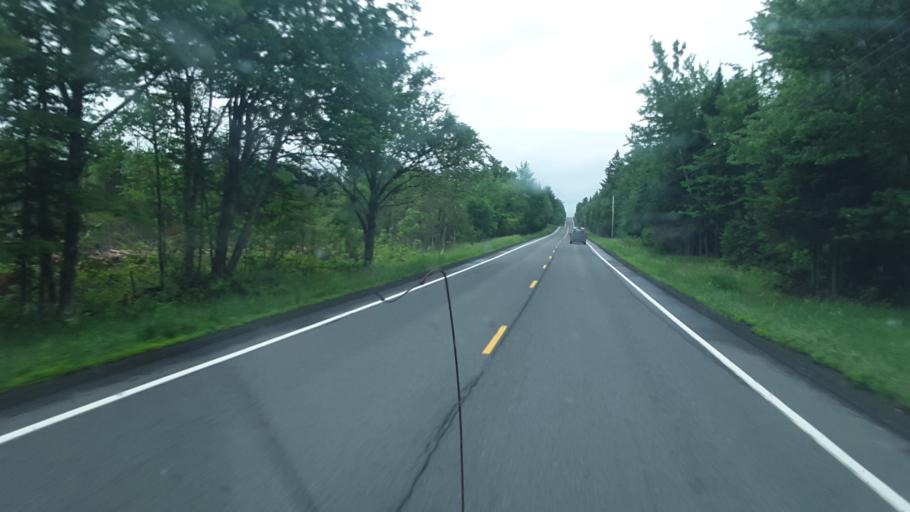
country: US
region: Maine
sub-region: Penobscot County
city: Patten
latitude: 46.3104
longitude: -68.3570
